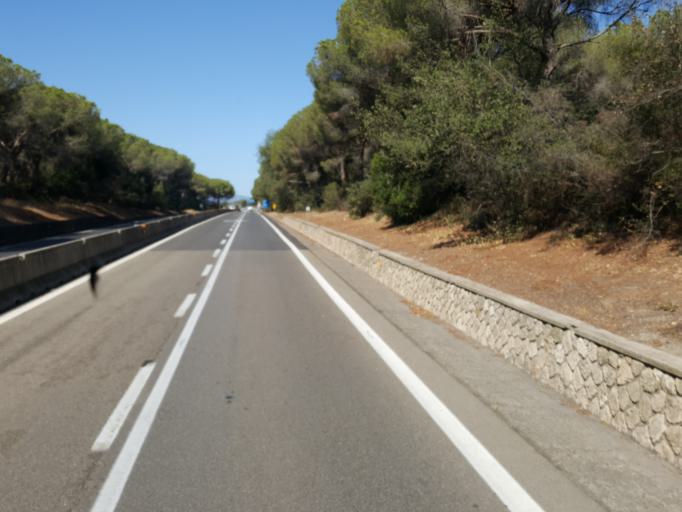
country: IT
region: Latium
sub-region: Provincia di Viterbo
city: Pescia Romana
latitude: 42.4142
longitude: 11.4688
